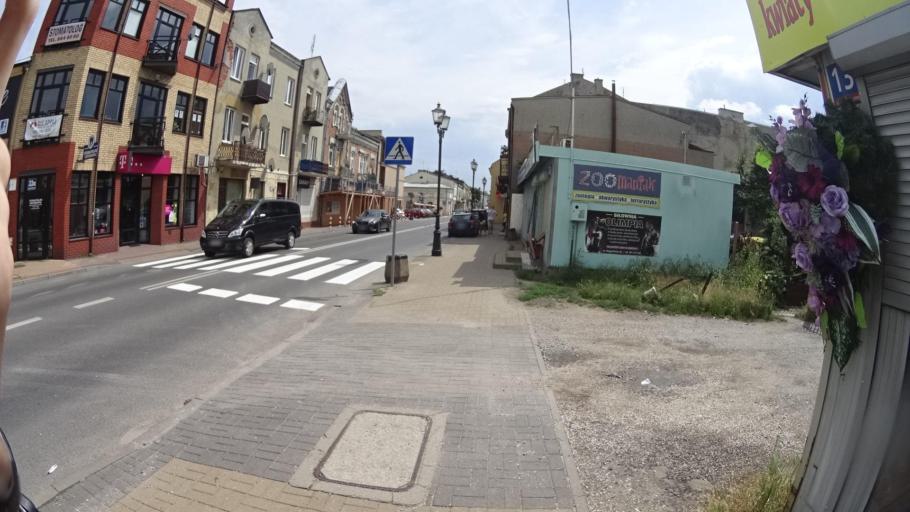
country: PL
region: Masovian Voivodeship
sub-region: Powiat grojecki
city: Grojec
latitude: 51.8677
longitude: 20.8656
